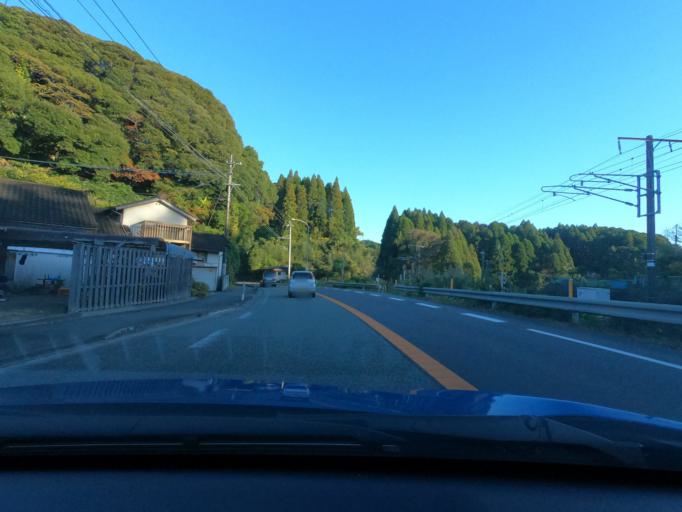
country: JP
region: Kagoshima
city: Satsumasendai
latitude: 31.8488
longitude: 130.2447
